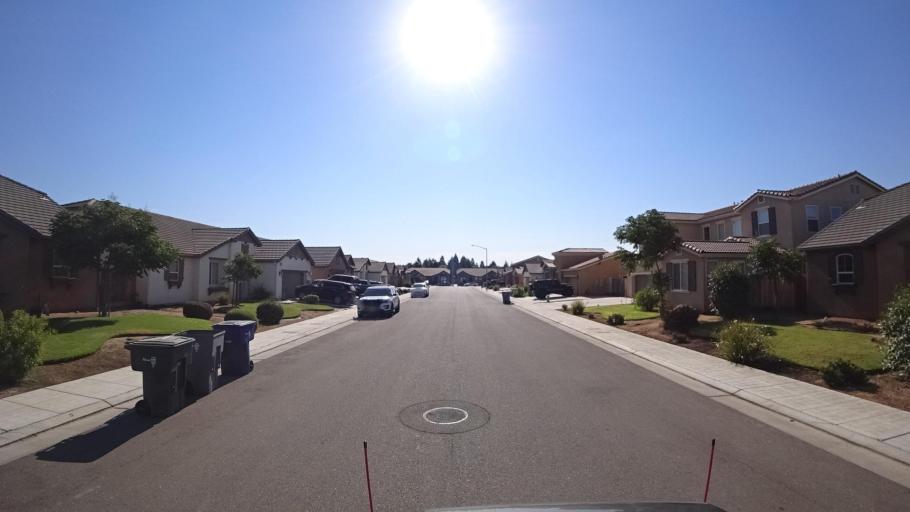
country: US
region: California
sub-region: Fresno County
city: Tarpey Village
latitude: 36.7858
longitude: -119.6523
